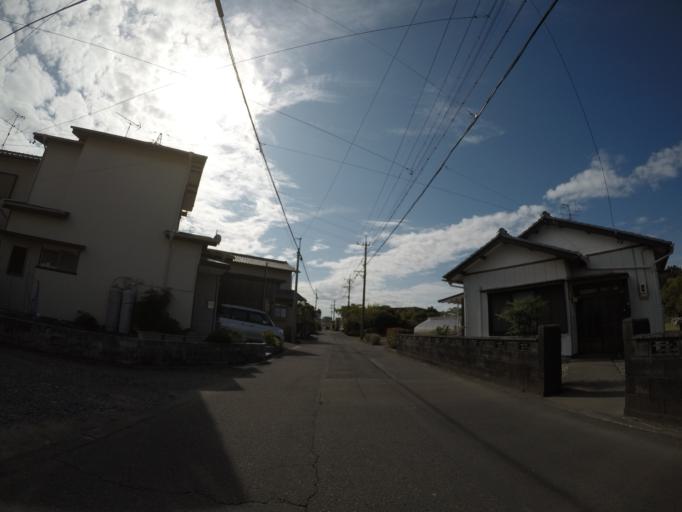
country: JP
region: Shizuoka
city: Fujieda
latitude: 34.8316
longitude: 138.2935
